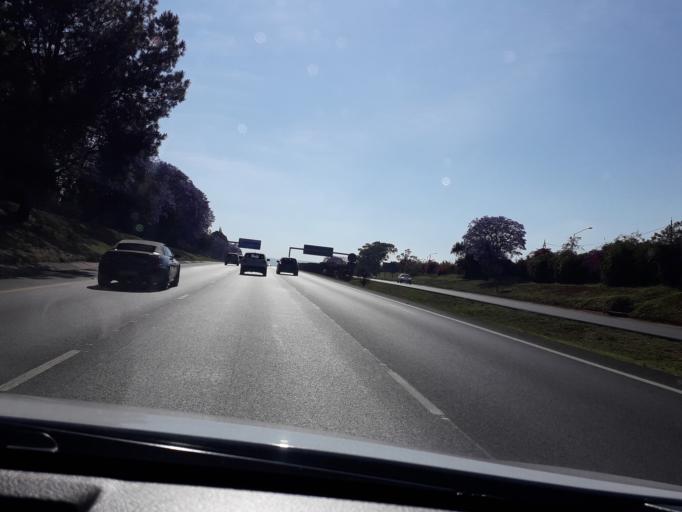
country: ZA
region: Gauteng
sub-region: City of Tshwane Metropolitan Municipality
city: Pretoria
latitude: -25.7530
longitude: 28.3136
